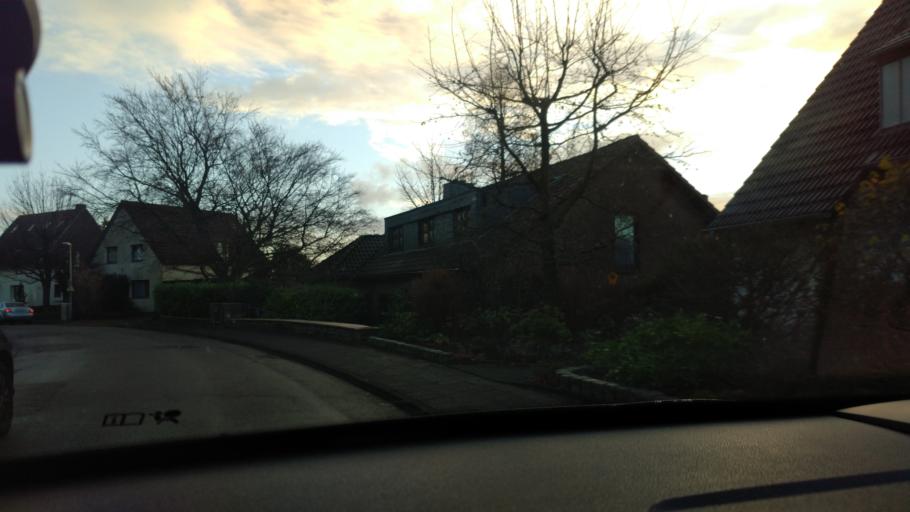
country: DE
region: North Rhine-Westphalia
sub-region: Regierungsbezirk Dusseldorf
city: Muelheim (Ruhr)
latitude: 51.4026
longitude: 6.8536
